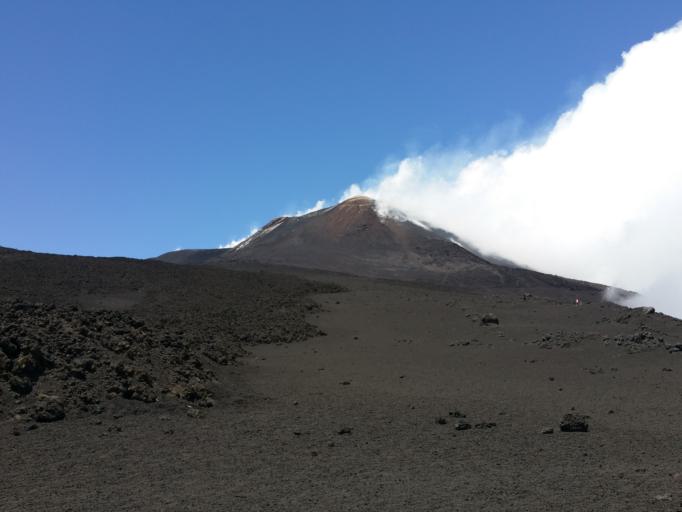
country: IT
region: Sicily
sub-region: Catania
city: Milo
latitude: 37.7324
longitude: 15.0091
